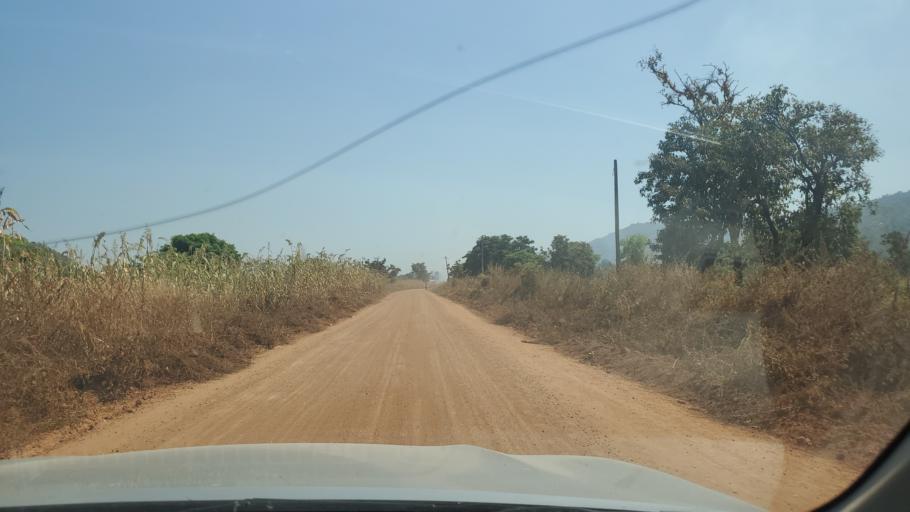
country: NG
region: Niger
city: Gawu Babangida
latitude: 9.2220
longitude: 6.8404
